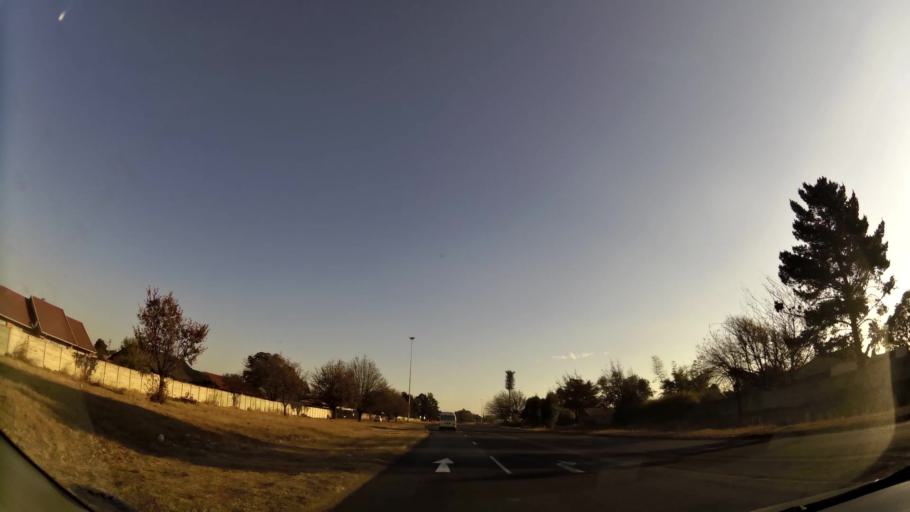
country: ZA
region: Gauteng
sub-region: West Rand District Municipality
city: Randfontein
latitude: -26.2086
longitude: 27.6579
